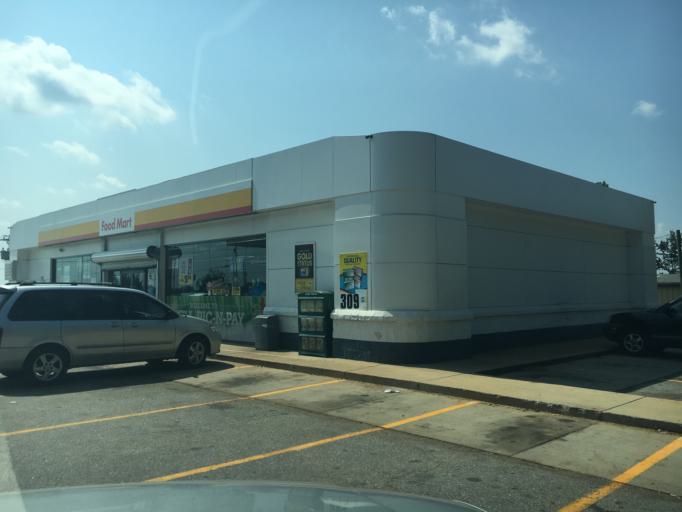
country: US
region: South Carolina
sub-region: Anderson County
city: Powdersville
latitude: 34.7614
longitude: -82.4756
